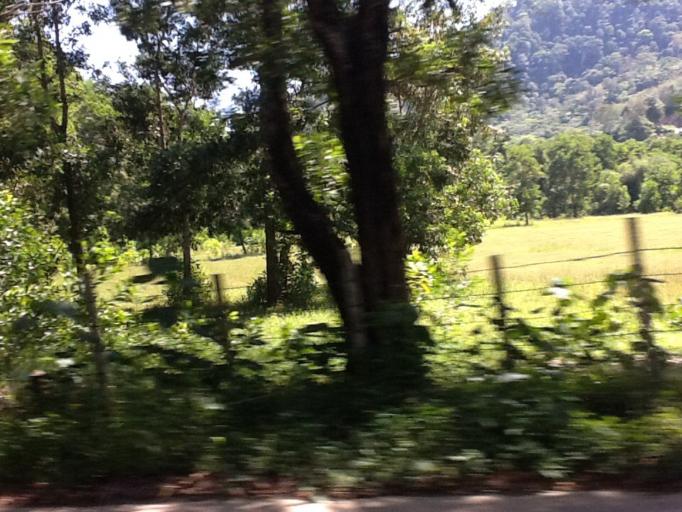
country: TH
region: Phuket
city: Ban Ko Kaeo
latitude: 7.9482
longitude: 98.3650
